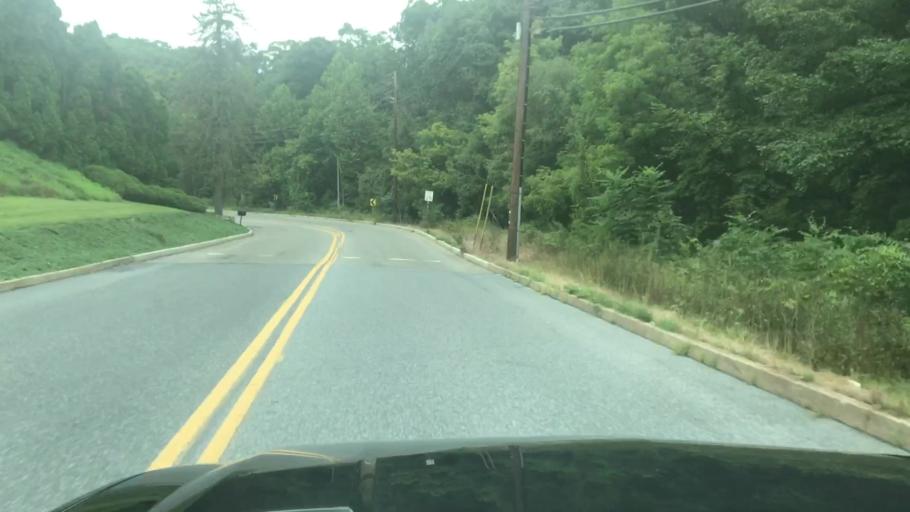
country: US
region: Pennsylvania
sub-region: Dauphin County
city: Progress
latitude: 40.3082
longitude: -76.8473
